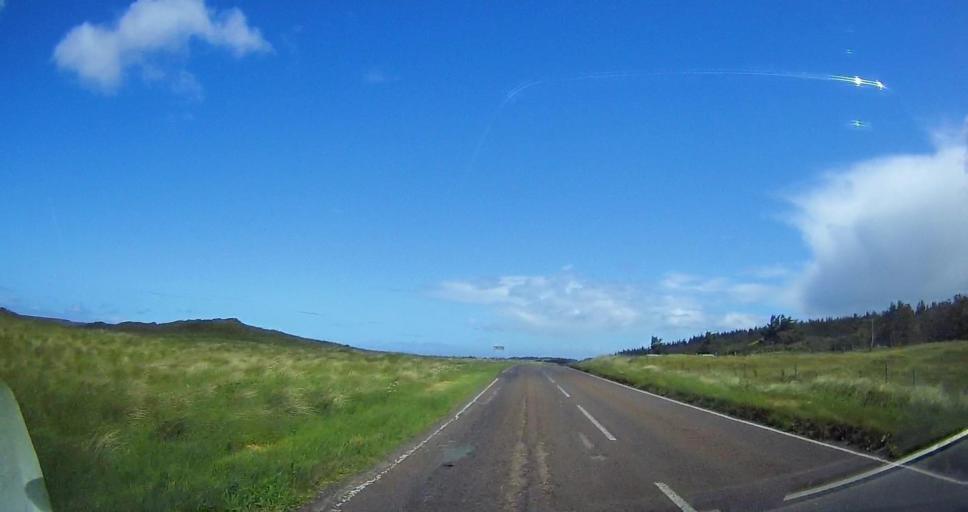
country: GB
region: Scotland
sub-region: Highland
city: Thurso
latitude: 58.6083
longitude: -3.3437
